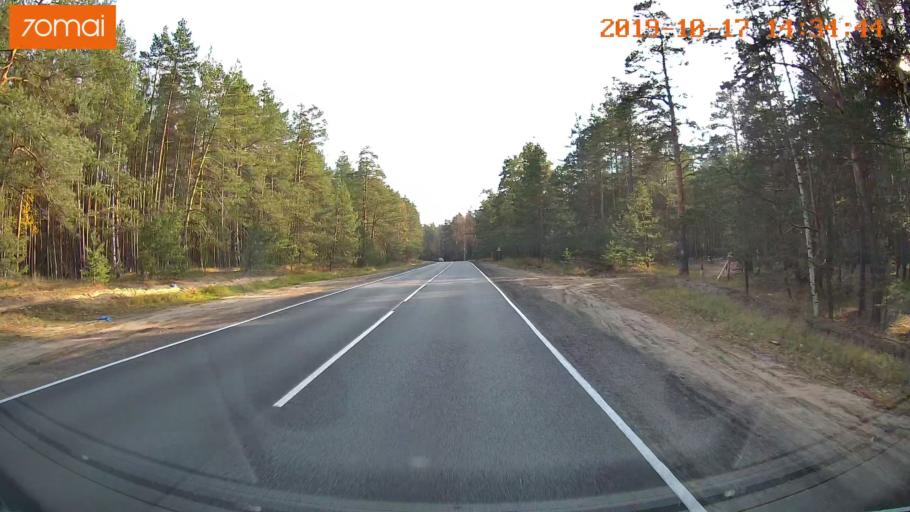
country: RU
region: Rjazan
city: Solotcha
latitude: 54.9084
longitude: 39.9989
